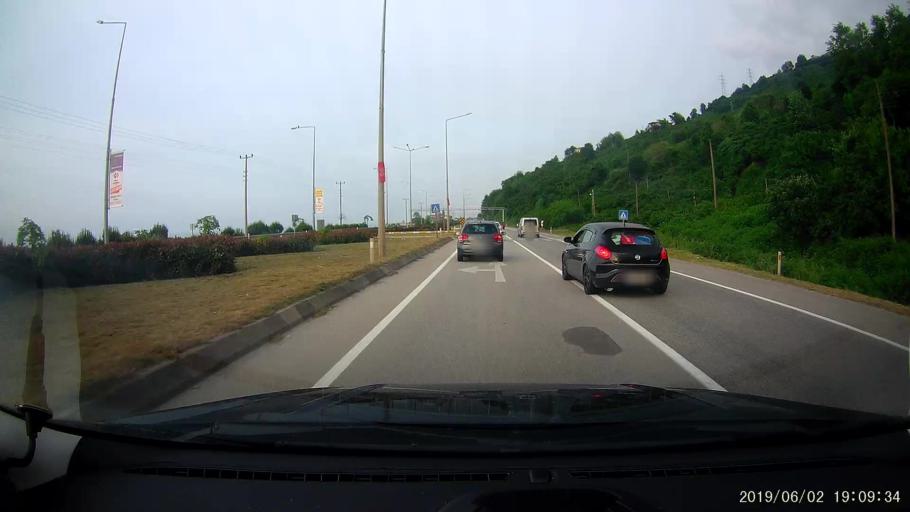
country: TR
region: Ordu
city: Gulyali
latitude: 40.9726
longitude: 38.0305
